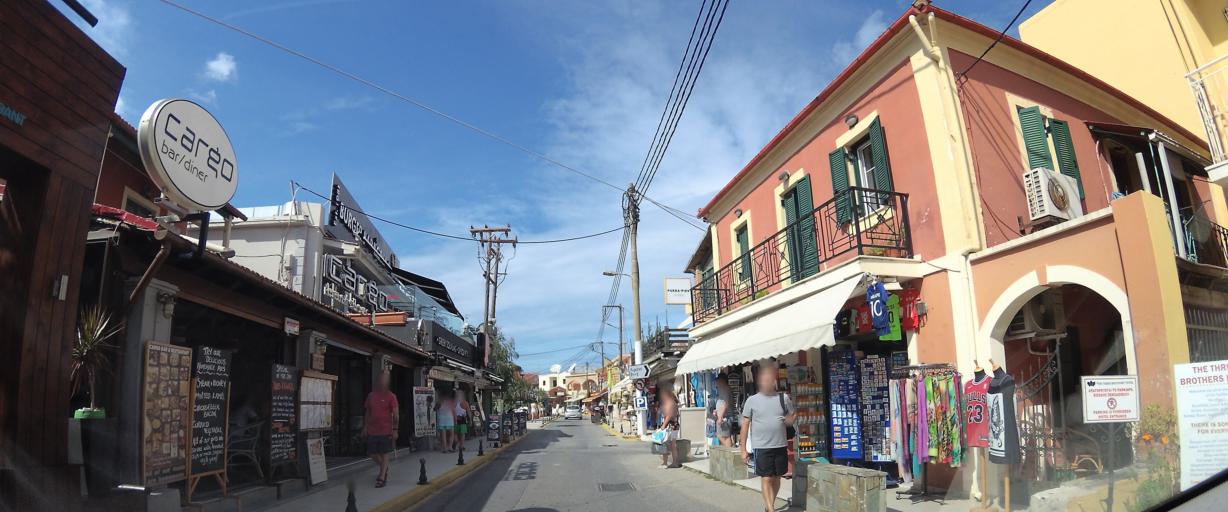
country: GR
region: Ionian Islands
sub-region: Nomos Kerkyras
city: Agios Georgis
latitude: 39.7917
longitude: 19.7080
